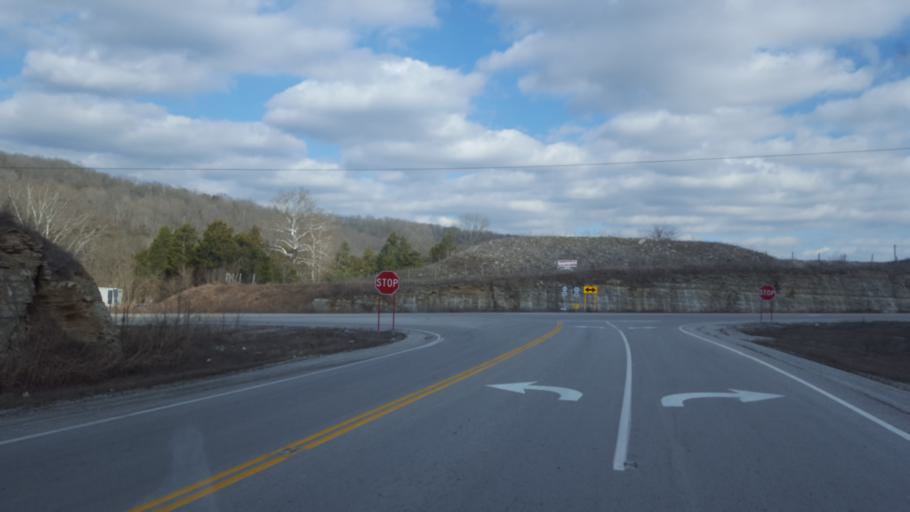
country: US
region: Kentucky
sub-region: Owen County
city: Owenton
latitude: 38.4727
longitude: -84.9503
